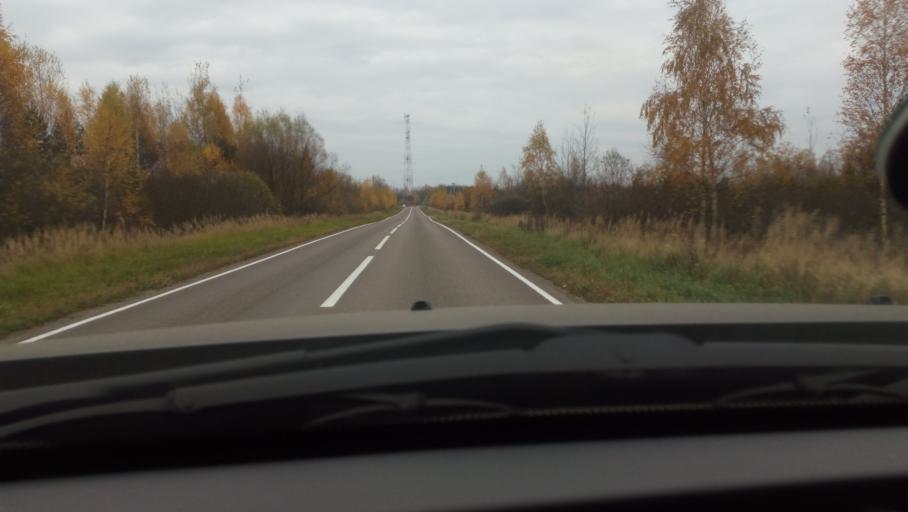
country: RU
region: Moskovskaya
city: Avsyunino
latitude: 55.5969
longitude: 39.2399
